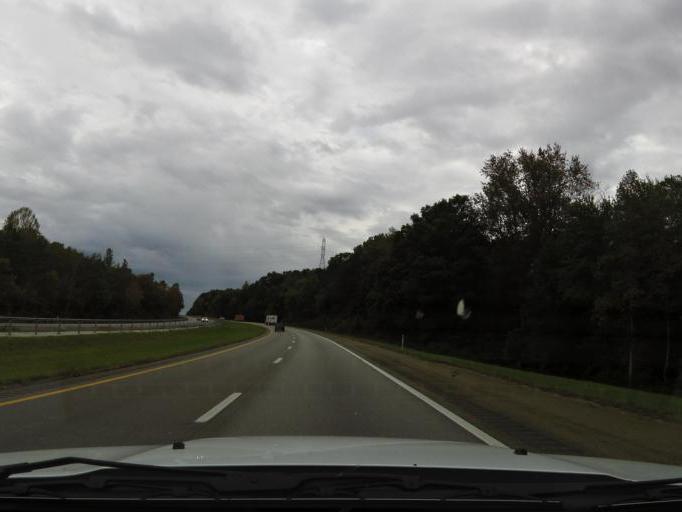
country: US
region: Kentucky
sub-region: Whitley County
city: Corbin
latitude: 36.8683
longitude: -84.1474
